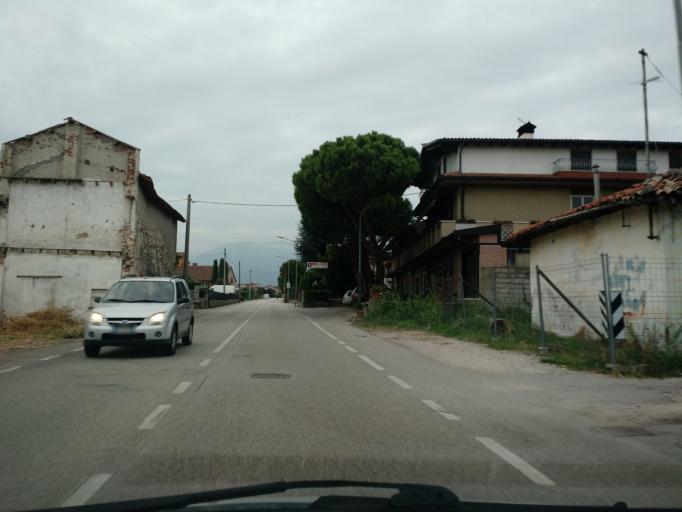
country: IT
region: Veneto
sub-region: Provincia di Vicenza
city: Thiene
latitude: 45.6974
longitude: 11.4738
